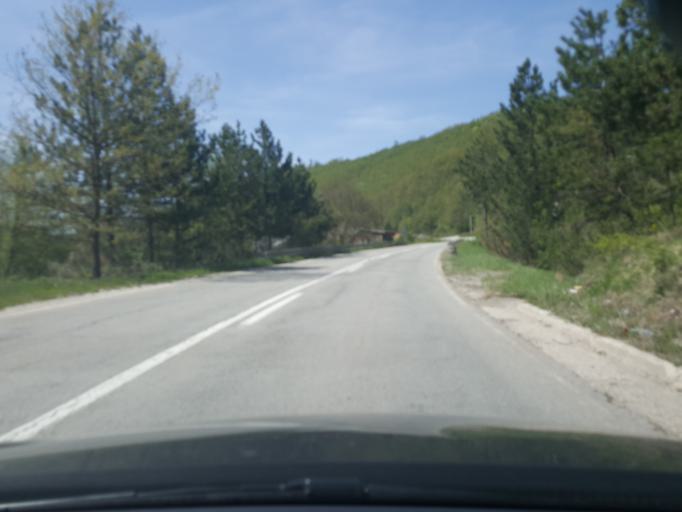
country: RS
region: Central Serbia
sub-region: Zlatiborski Okrug
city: Cajetina
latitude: 43.7924
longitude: 19.6572
